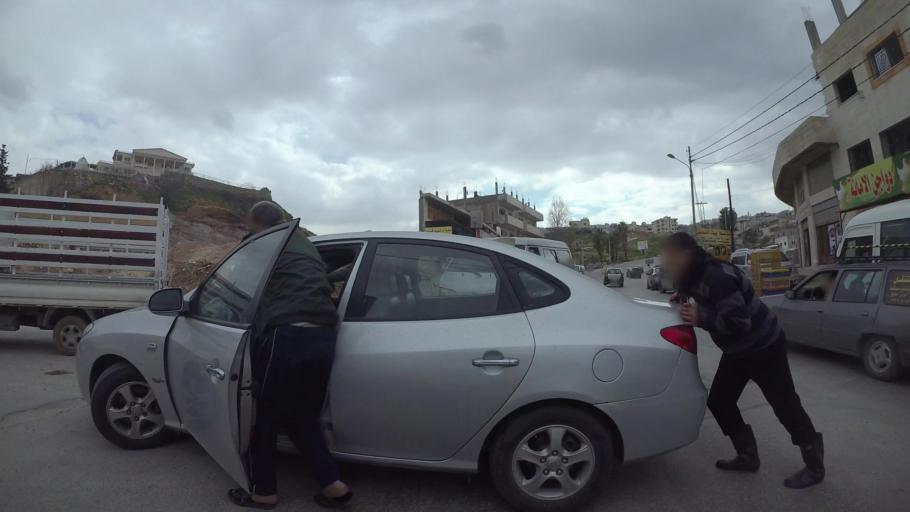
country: JO
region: Amman
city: Al Jubayhah
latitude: 32.0466
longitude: 35.8332
